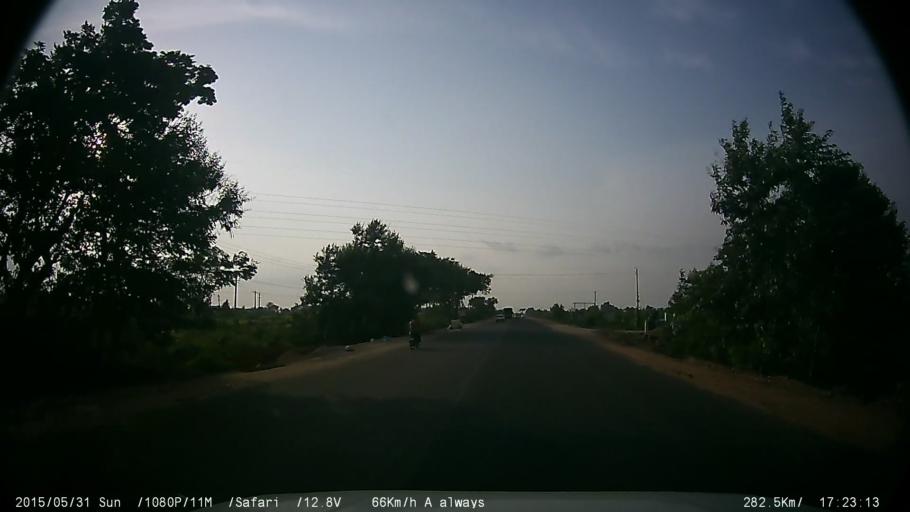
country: IN
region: Karnataka
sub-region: Chamrajnagar
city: Gundlupet
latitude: 11.8377
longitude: 76.6752
